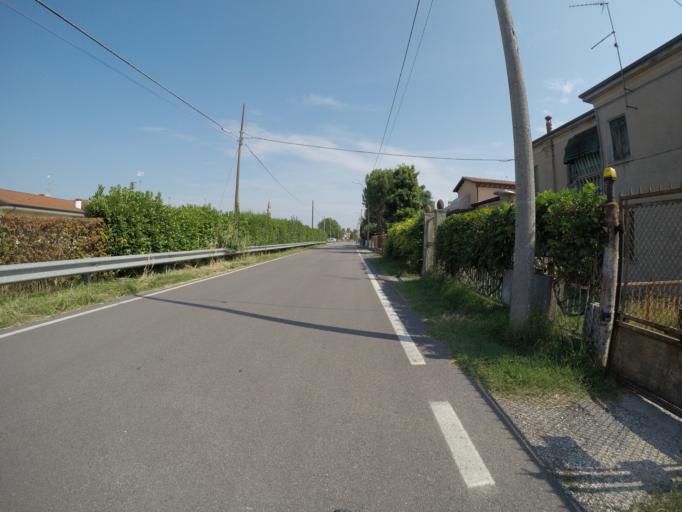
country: IT
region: Veneto
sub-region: Provincia di Rovigo
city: Lendinara
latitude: 45.0782
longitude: 11.6026
